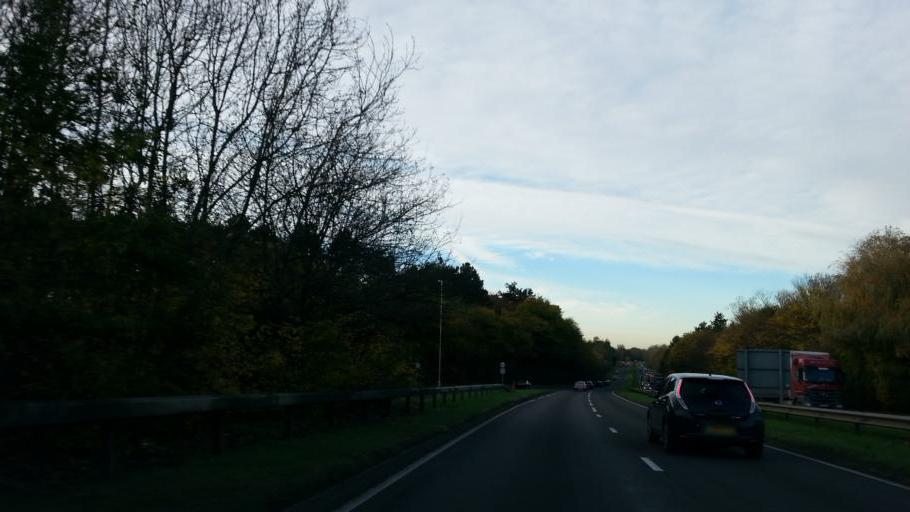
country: GB
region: England
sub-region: Northamptonshire
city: Northampton
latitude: 52.2574
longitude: -0.8388
